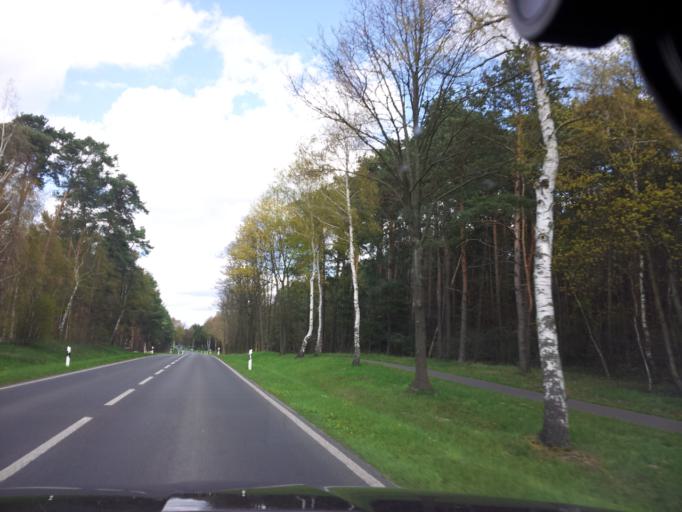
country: DE
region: Brandenburg
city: Rudnitz
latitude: 52.7026
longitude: 13.6114
